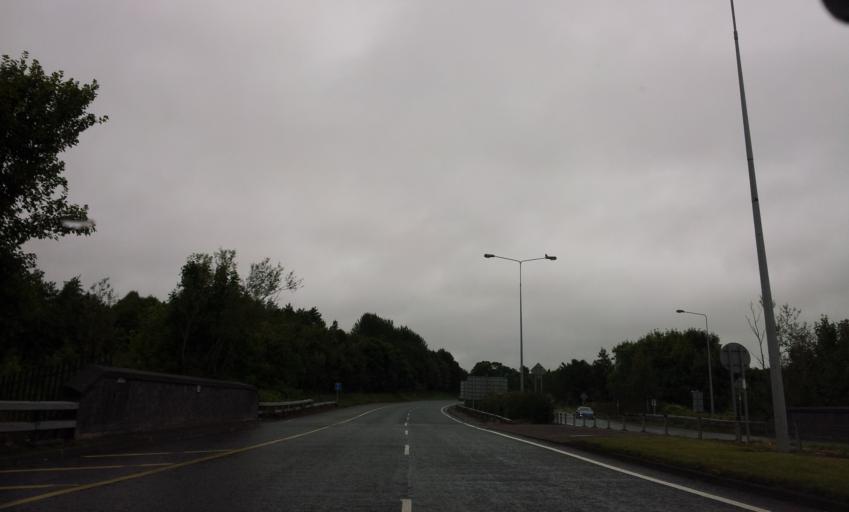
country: IE
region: Munster
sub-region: County Cork
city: Passage West
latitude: 51.9052
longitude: -8.3872
